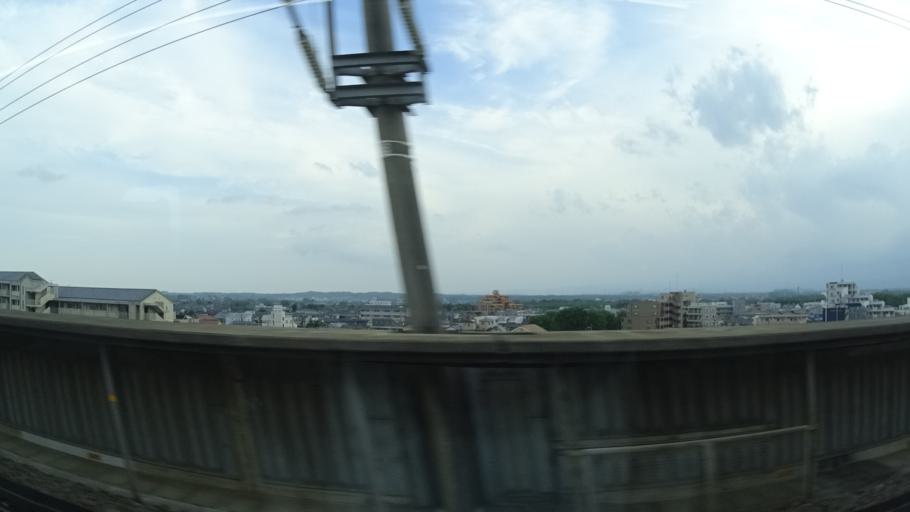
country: JP
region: Saitama
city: Kumagaya
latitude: 36.1377
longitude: 139.3944
